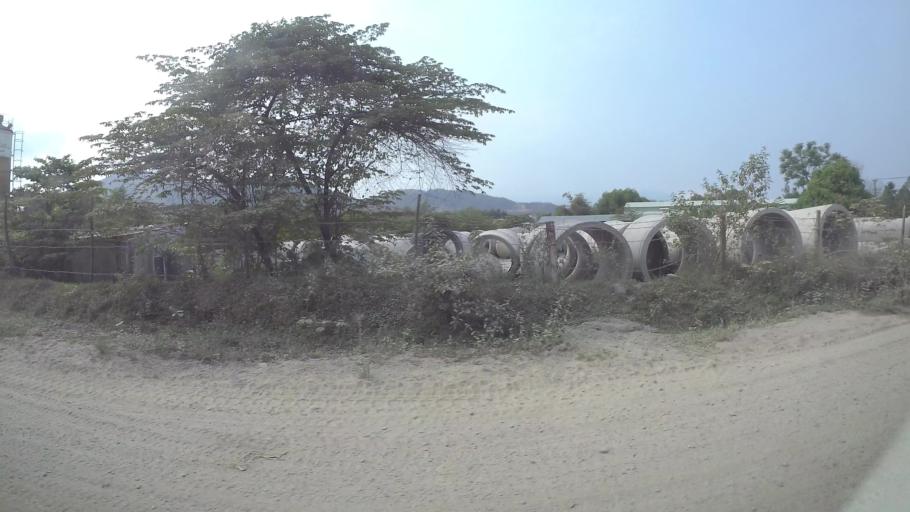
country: VN
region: Da Nang
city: Lien Chieu
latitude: 16.0451
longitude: 108.1511
